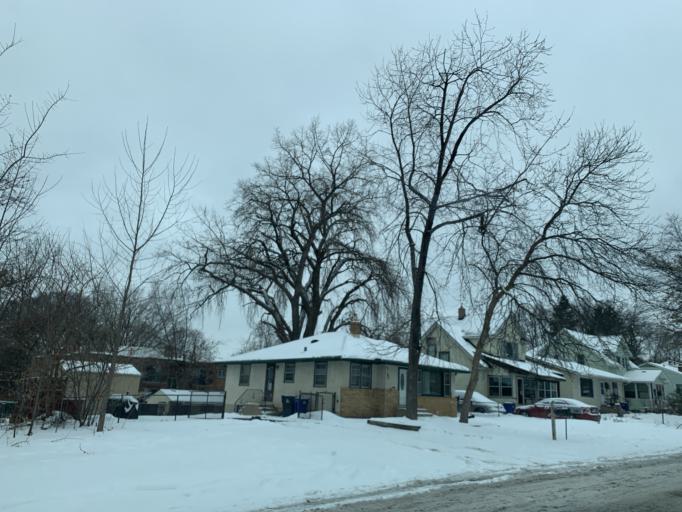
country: US
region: Minnesota
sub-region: Ramsey County
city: Little Canada
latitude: 44.9900
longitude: -93.1085
